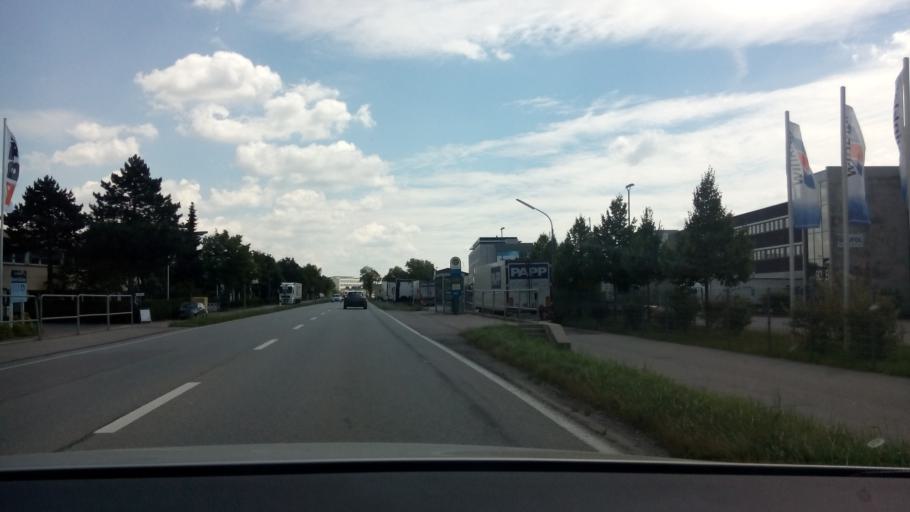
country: DE
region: Bavaria
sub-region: Upper Bavaria
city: Garching bei Munchen
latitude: 48.2499
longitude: 11.6219
